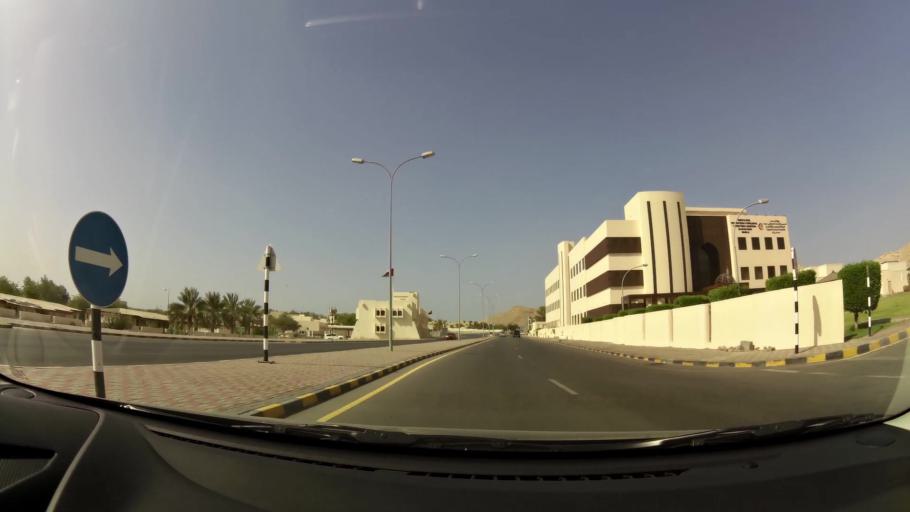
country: OM
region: Muhafazat Masqat
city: Muscat
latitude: 23.6134
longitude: 58.5158
